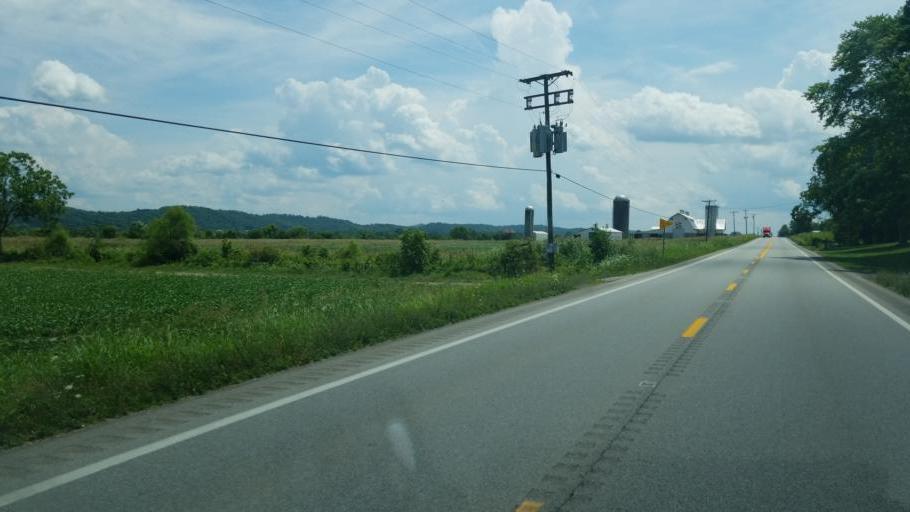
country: US
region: West Virginia
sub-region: Putnam County
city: Buffalo
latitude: 38.7301
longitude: -81.9730
